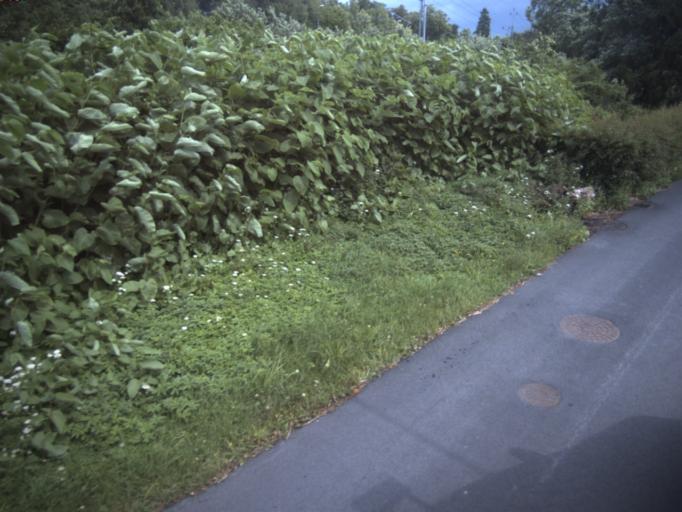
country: SE
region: Skane
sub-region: Helsingborg
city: Rydeback
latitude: 56.0197
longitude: 12.7453
